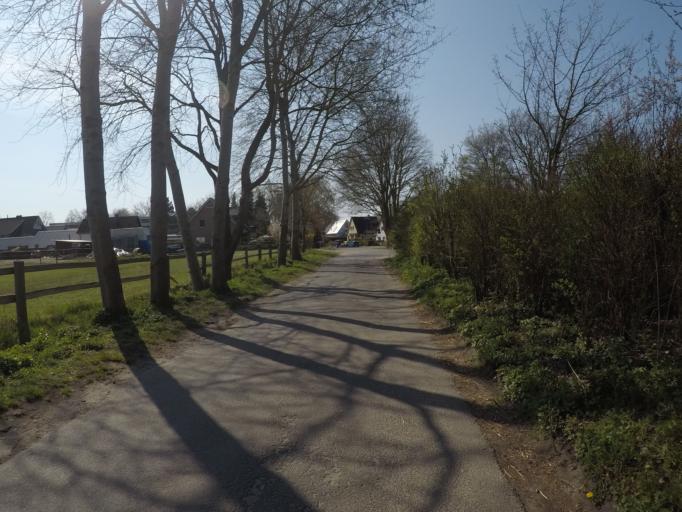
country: DE
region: Schleswig-Holstein
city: Halstenbek
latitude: 53.5857
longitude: 9.8180
